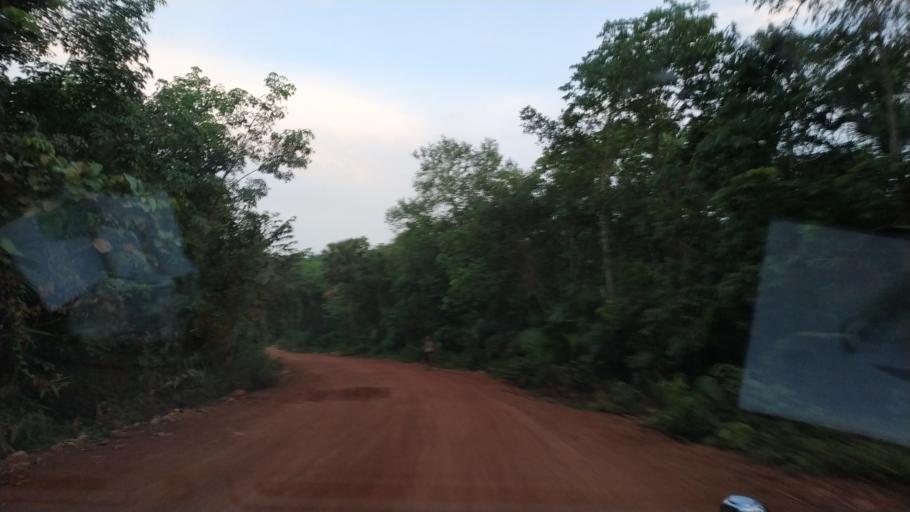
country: MM
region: Mon
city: Kyaikto
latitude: 17.4254
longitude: 97.0452
